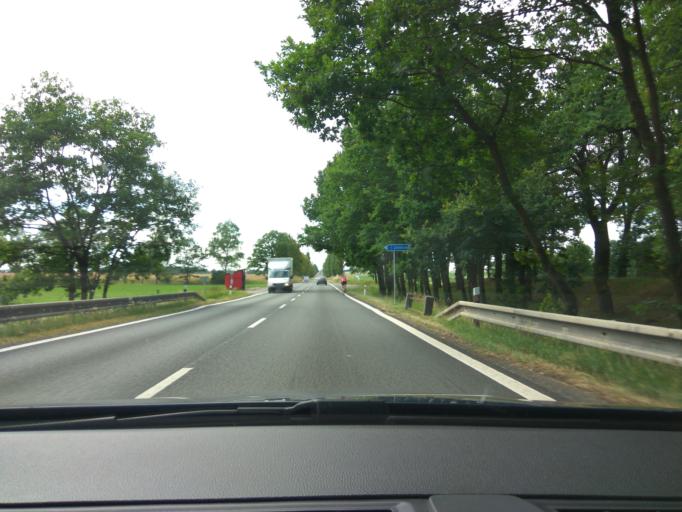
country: CZ
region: Jihocesky
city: Kovarov
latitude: 49.4945
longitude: 14.2320
